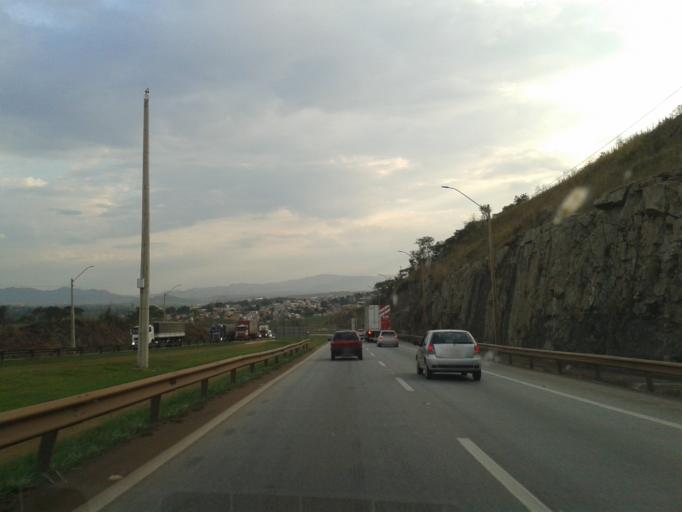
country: BR
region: Minas Gerais
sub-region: Betim
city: Betim
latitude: -19.9629
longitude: -44.1574
